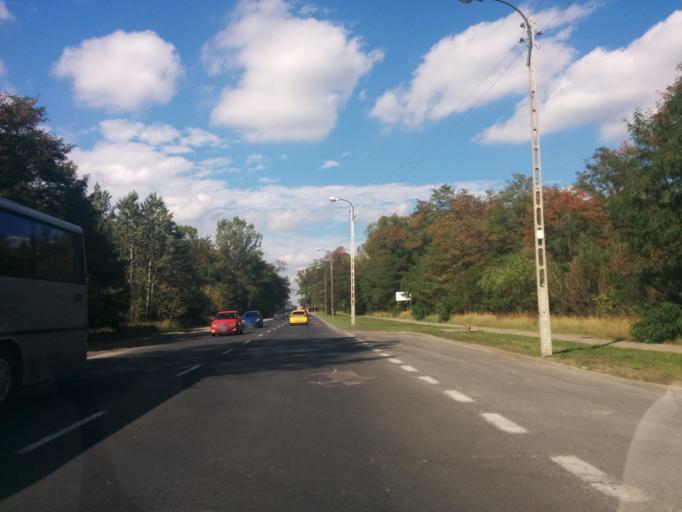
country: PL
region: Masovian Voivodeship
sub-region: Warszawa
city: Bialoleka
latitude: 52.3097
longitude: 21.0048
